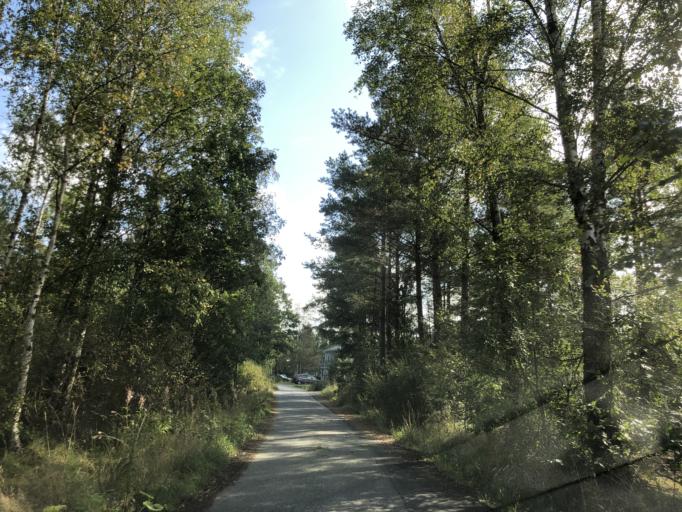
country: SE
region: Vaestra Goetaland
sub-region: Goteborg
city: Torslanda
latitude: 57.7384
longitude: 11.8341
